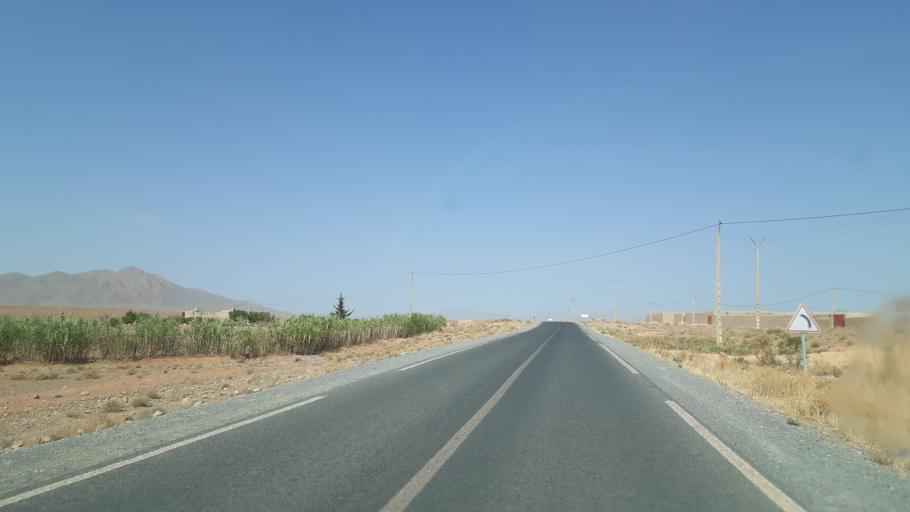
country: MA
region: Meknes-Tafilalet
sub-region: Errachidia
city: Amouguer
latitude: 32.2341
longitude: -4.6393
